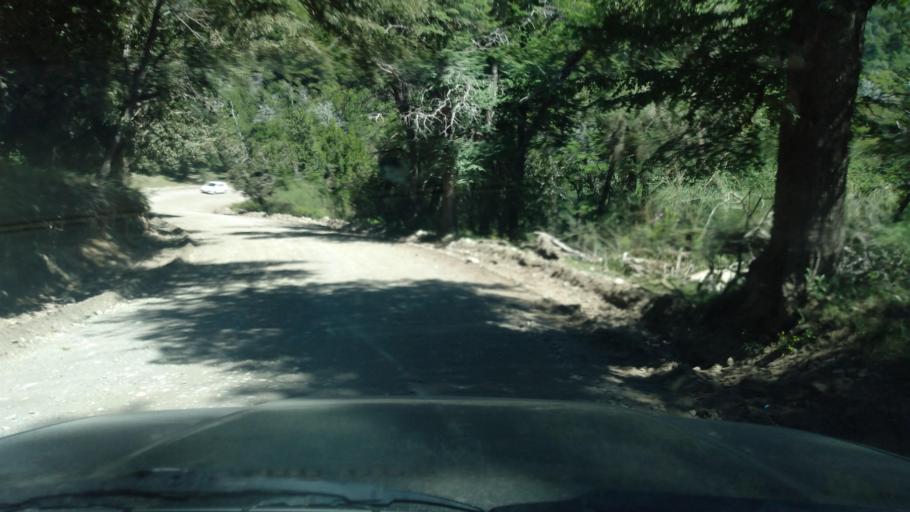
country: AR
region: Neuquen
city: Villa La Angostura
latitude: -40.6212
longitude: -71.5794
